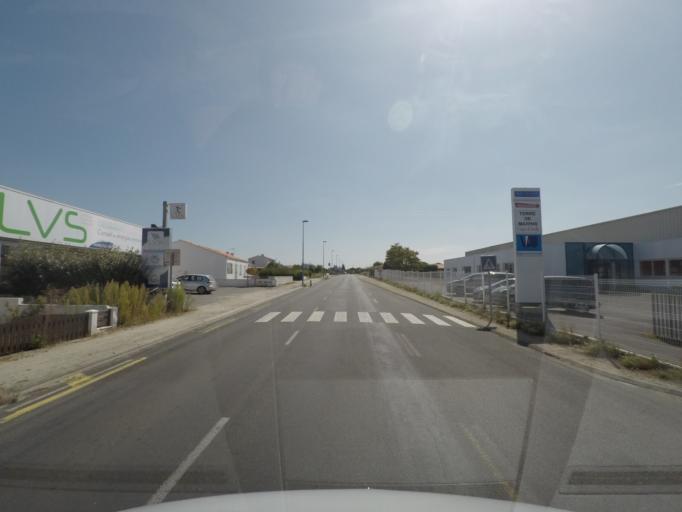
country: FR
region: Pays de la Loire
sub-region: Departement de la Vendee
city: Beauvoir-sur-Mer
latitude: 46.9104
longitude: -2.0337
